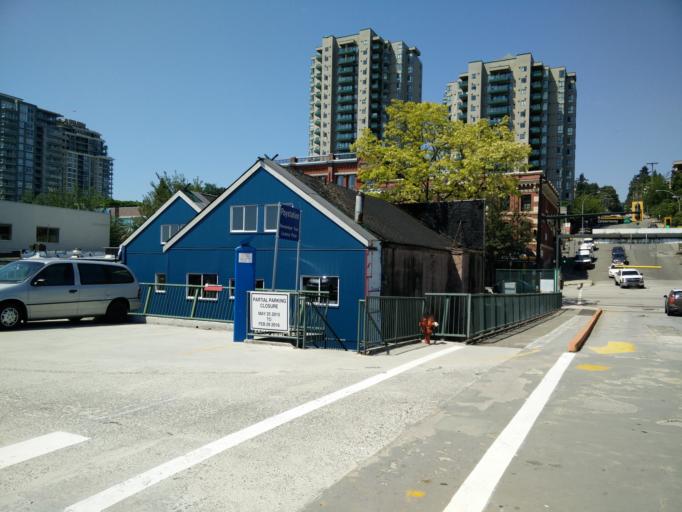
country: CA
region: British Columbia
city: New Westminster
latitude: 49.2043
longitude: -122.9048
